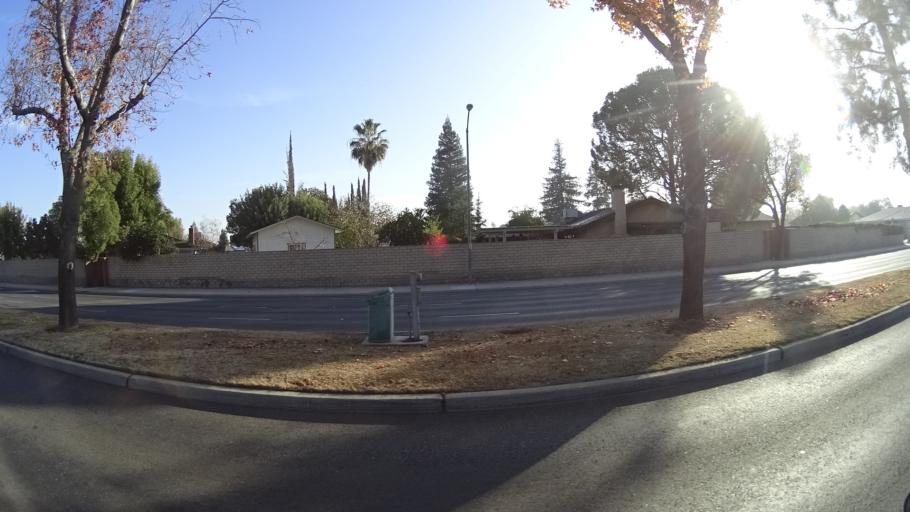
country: US
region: California
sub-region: Kern County
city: Greenacres
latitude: 35.3353
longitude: -119.0923
